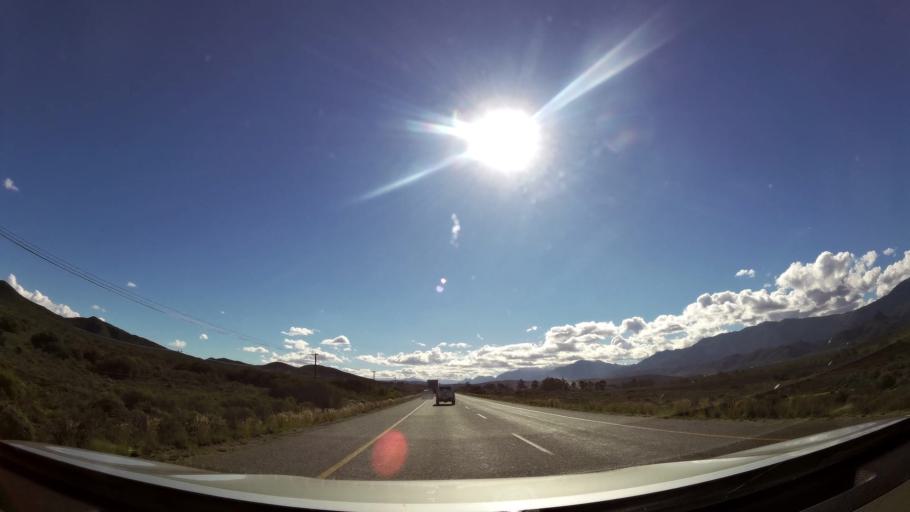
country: ZA
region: Western Cape
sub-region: Cape Winelands District Municipality
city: Ashton
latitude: -33.7679
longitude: 19.7471
